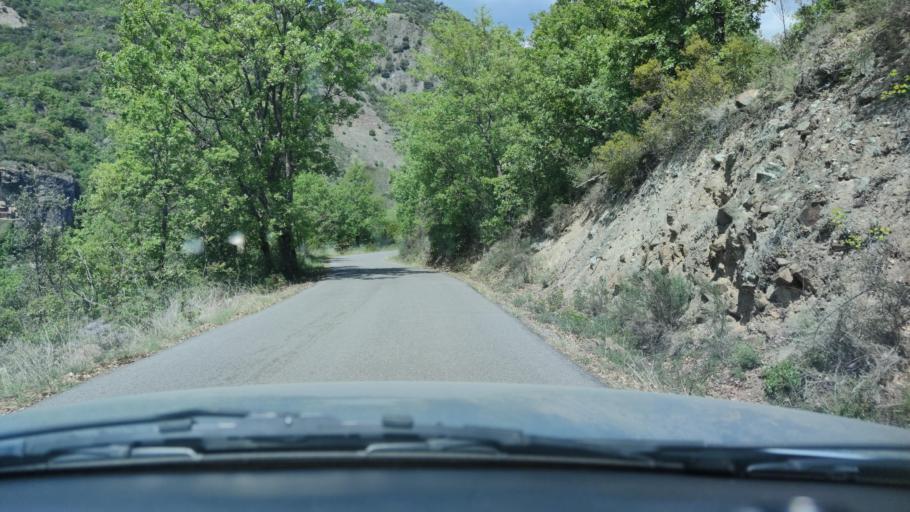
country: ES
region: Catalonia
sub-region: Provincia de Lleida
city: Sort
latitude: 42.3136
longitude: 1.0630
